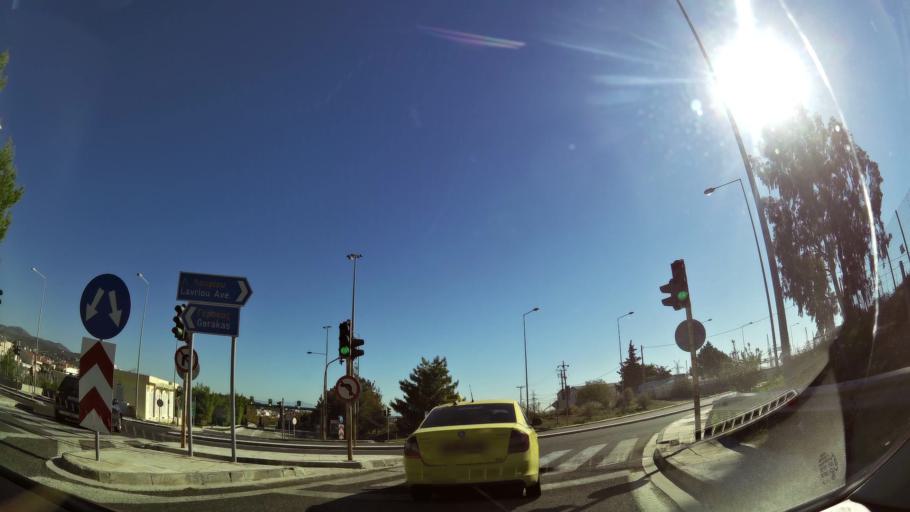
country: GR
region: Attica
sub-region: Nomarchia Anatolikis Attikis
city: Leondarion
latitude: 37.9969
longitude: 23.8499
